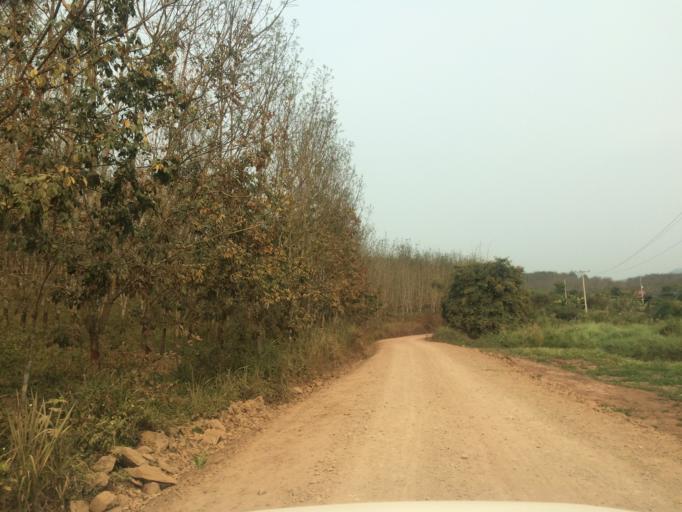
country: LA
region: Loungnamtha
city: Muang Nale
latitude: 20.4200
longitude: 101.6863
